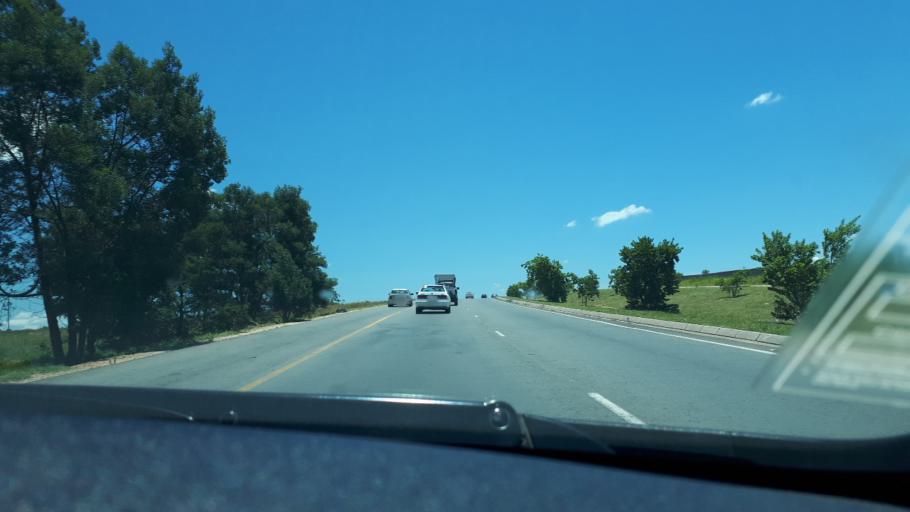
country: ZA
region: Gauteng
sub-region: West Rand District Municipality
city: Muldersdriseloop
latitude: -26.0026
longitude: 27.9280
